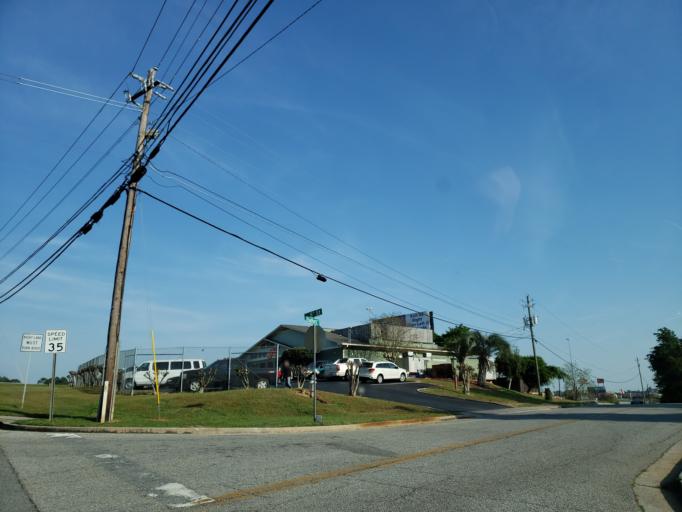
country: US
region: Georgia
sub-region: Tift County
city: Tifton
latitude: 31.4636
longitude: -83.5315
